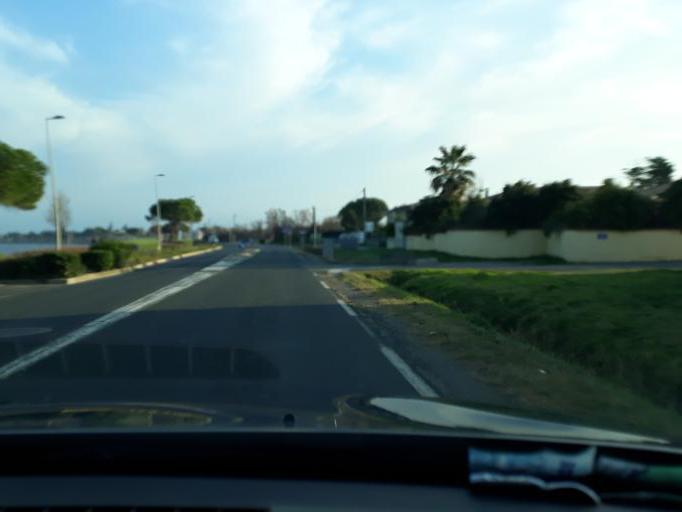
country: FR
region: Languedoc-Roussillon
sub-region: Departement de l'Herault
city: Marseillan
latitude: 43.3456
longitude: 3.5315
